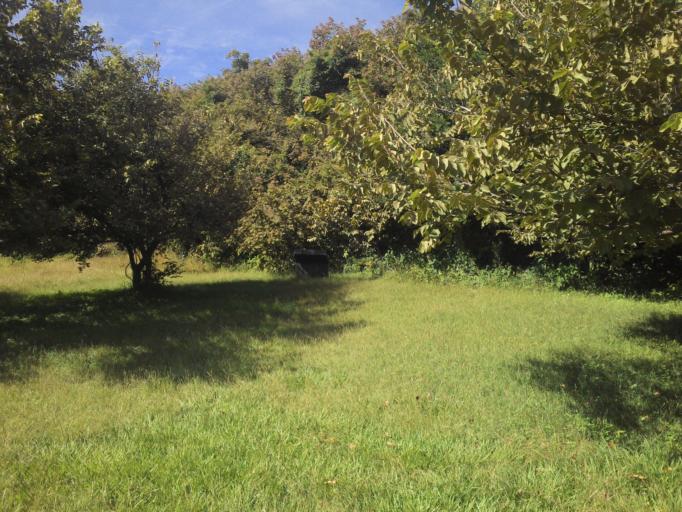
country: MX
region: Jalisco
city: Teuchitlan
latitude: 20.6958
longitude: -103.8347
